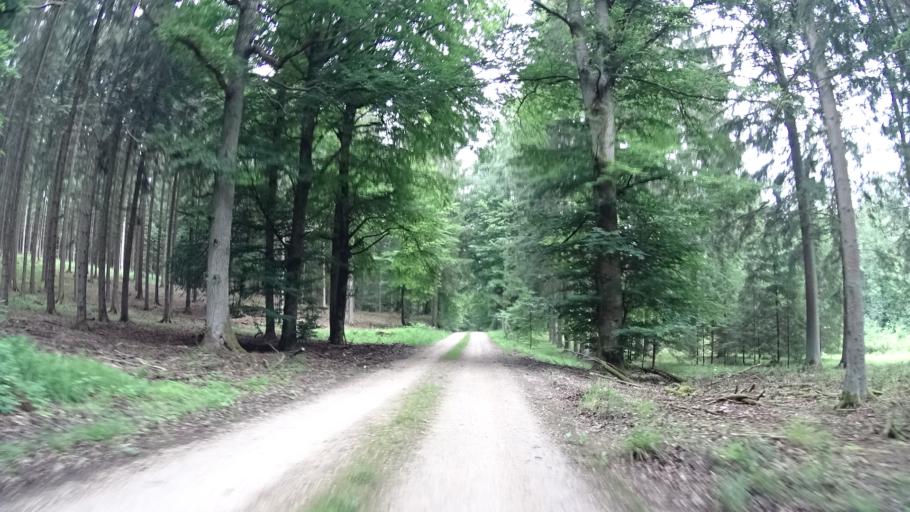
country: DE
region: Bavaria
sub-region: Upper Bavaria
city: Oberdolling
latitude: 48.9017
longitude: 11.5444
